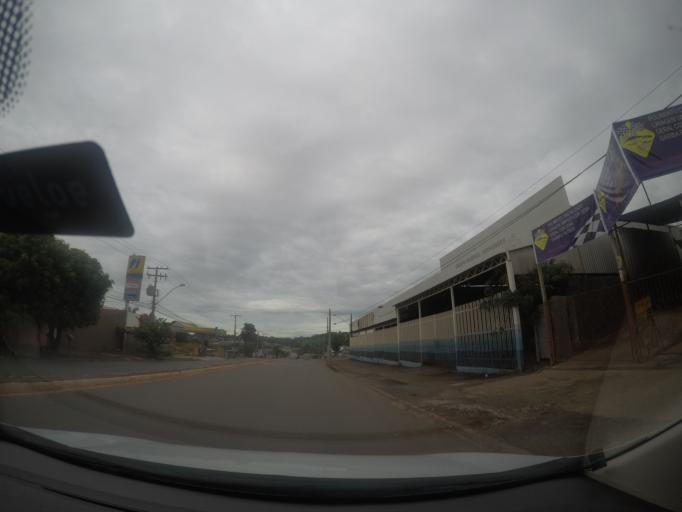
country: BR
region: Goias
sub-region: Goiania
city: Goiania
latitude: -16.6278
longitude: -49.2848
